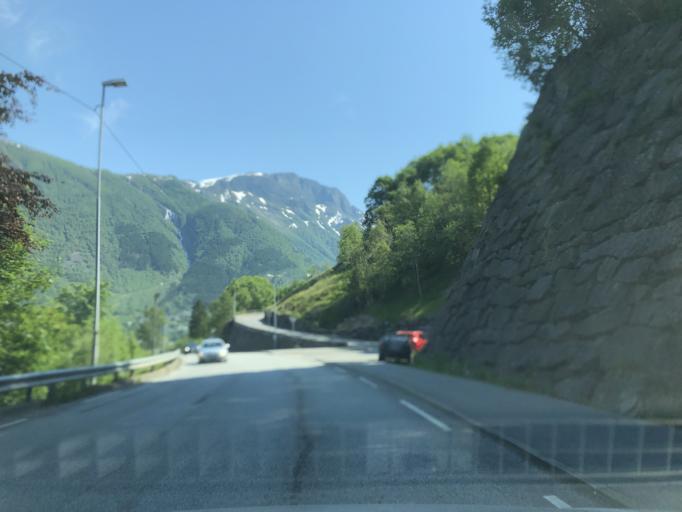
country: NO
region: Hordaland
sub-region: Odda
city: Odda
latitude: 60.0765
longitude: 6.5323
